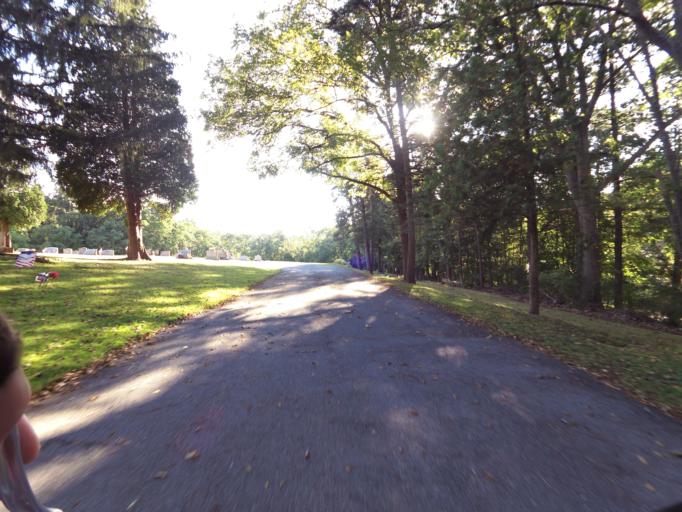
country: US
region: Pennsylvania
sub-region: Perry County
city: Marysville
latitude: 40.3388
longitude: -76.9393
